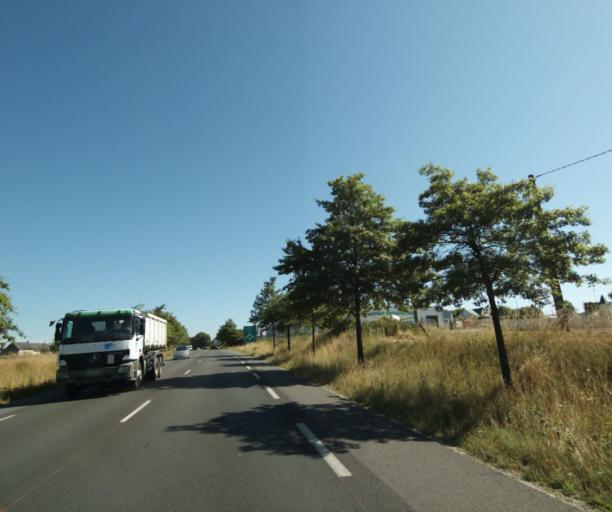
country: FR
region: Pays de la Loire
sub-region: Departement de la Mayenne
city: Bonchamp-les-Laval
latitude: 48.0686
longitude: -0.7313
